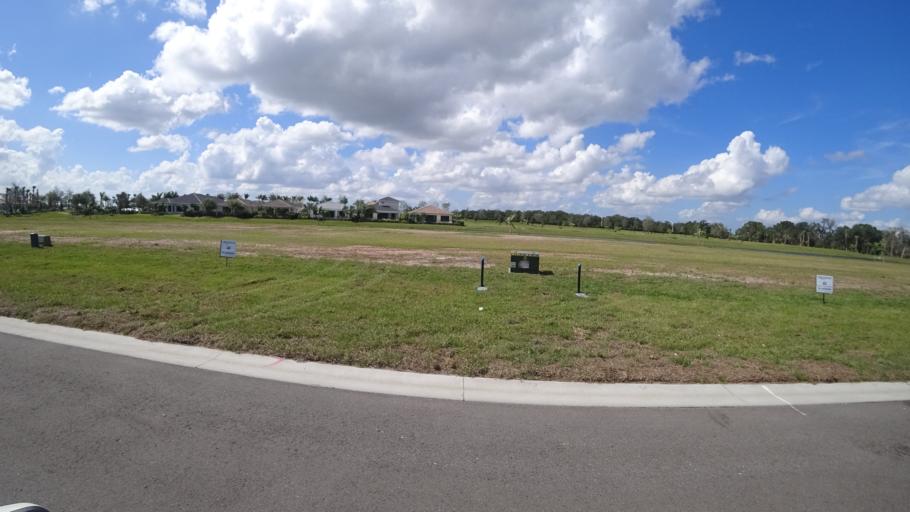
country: US
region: Florida
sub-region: Sarasota County
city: The Meadows
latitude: 27.4512
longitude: -82.3689
